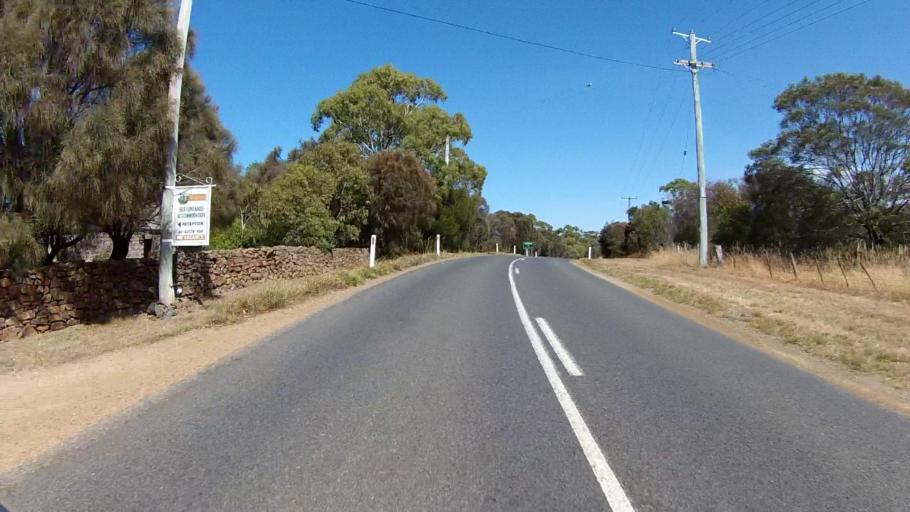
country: AU
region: Tasmania
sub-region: Sorell
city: Sorell
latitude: -42.1388
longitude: 148.0708
